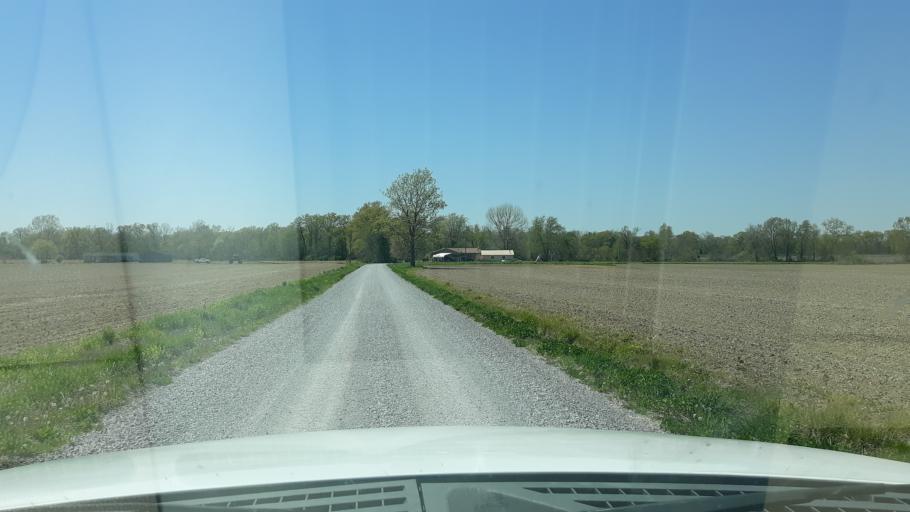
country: US
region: Illinois
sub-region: Saline County
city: Harrisburg
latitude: 37.8923
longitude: -88.6759
